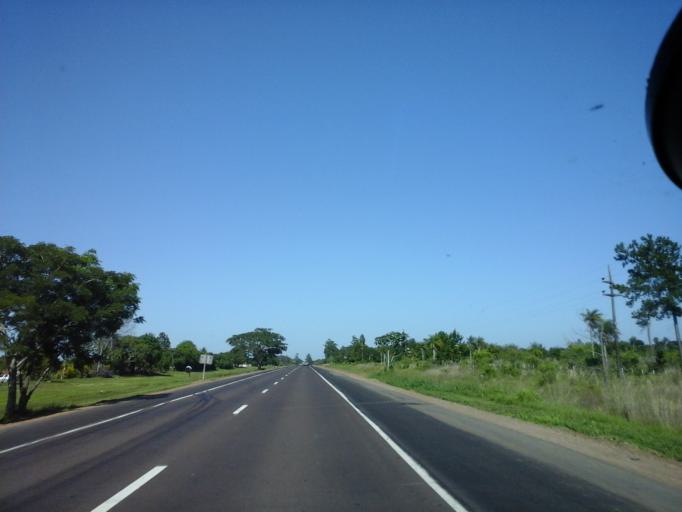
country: AR
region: Corrientes
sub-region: Departamento de Itati
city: Itati
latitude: -27.3669
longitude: -58.3482
